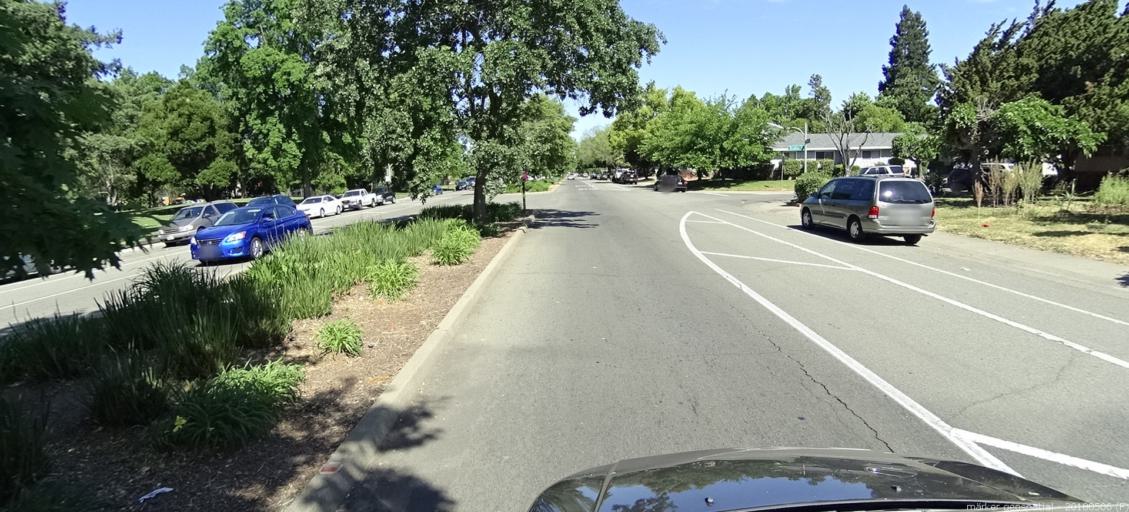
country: US
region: California
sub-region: Sacramento County
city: Parkway
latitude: 38.4823
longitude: -121.4425
